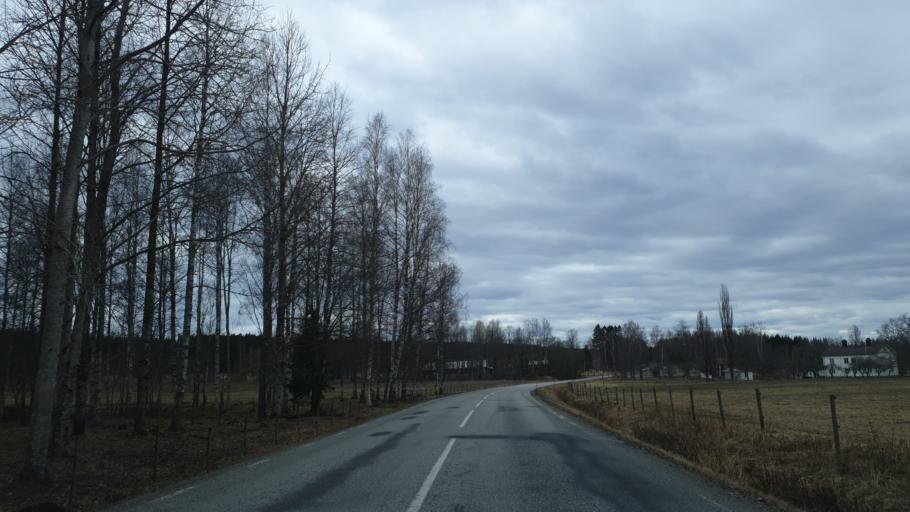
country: SE
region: OErebro
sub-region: Nora Kommun
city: As
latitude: 59.5841
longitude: 14.9599
